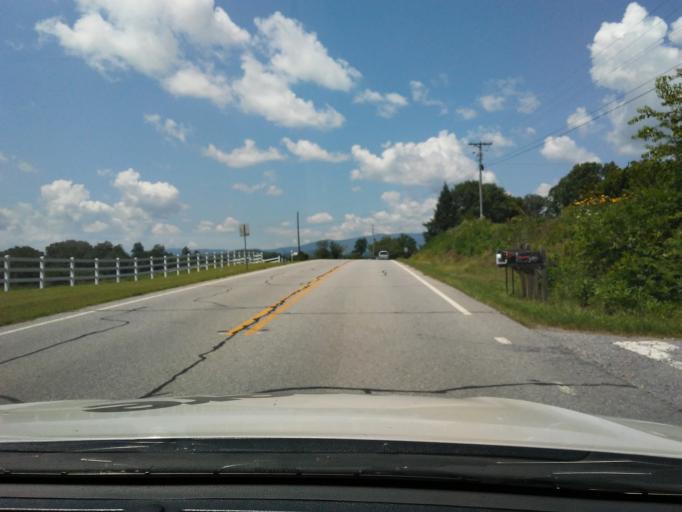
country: US
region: Georgia
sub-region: Towns County
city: Hiawassee
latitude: 34.9852
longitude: -83.7550
